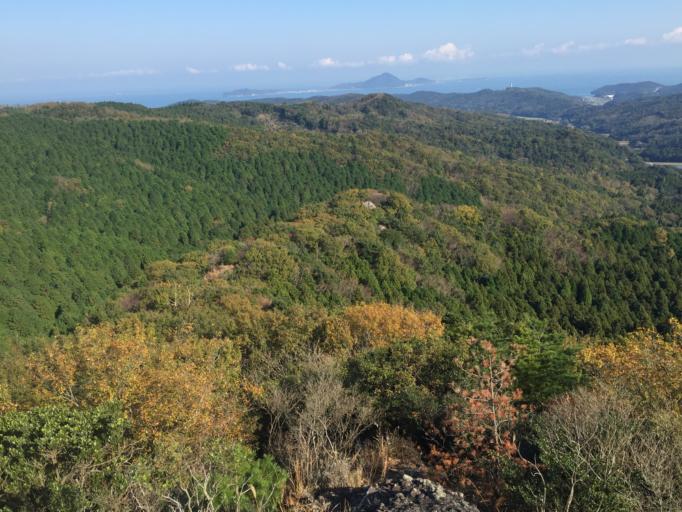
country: JP
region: Oita
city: Bungo-Takada-shi
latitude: 33.6270
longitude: 131.6049
